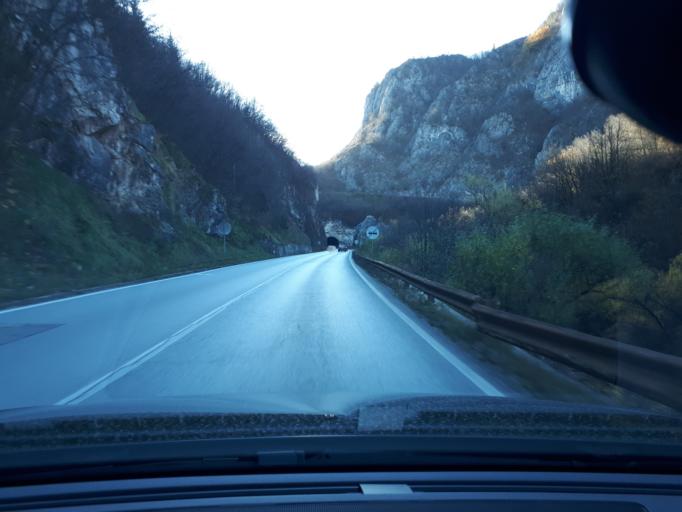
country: BA
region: Republika Srpska
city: Pale
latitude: 43.8522
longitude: 18.5220
